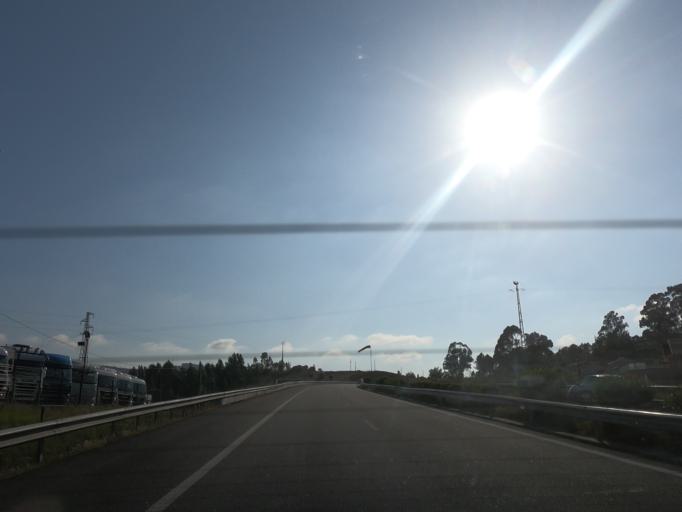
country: PT
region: Porto
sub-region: Valongo
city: Campo
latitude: 41.1878
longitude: -8.4674
